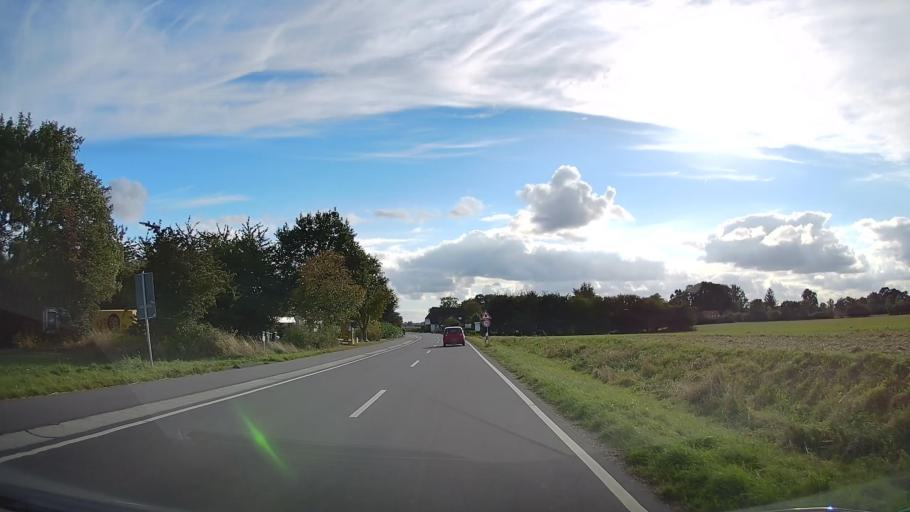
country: DE
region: Schleswig-Holstein
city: Pommerby
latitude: 54.7624
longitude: 9.9456
